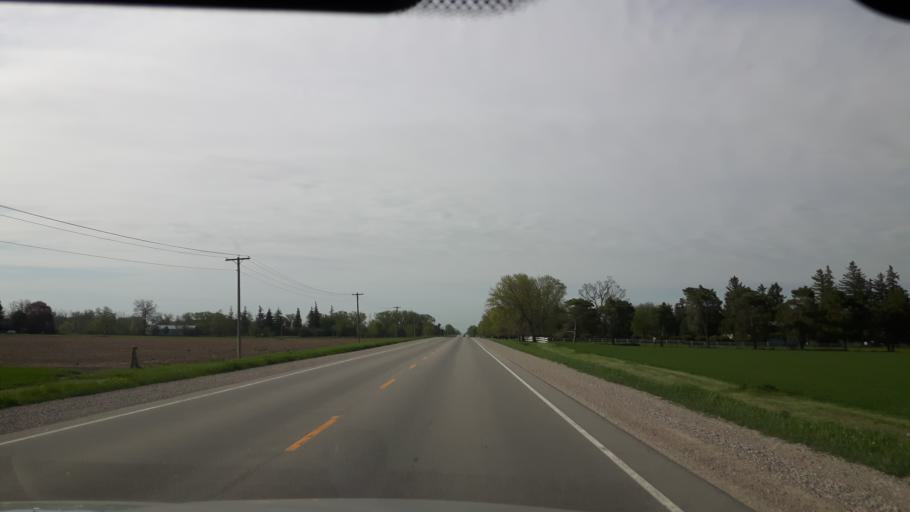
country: CA
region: Ontario
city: South Huron
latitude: 43.4241
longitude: -81.4965
